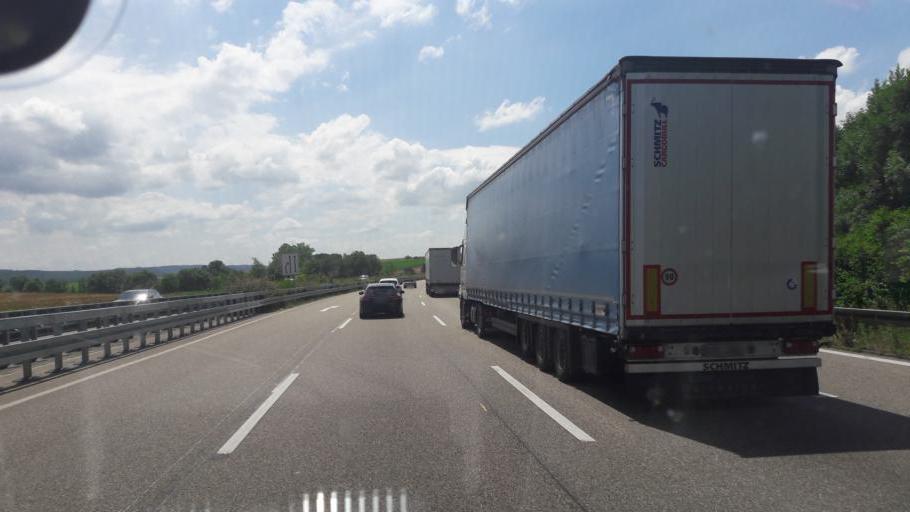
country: DE
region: Baden-Wuerttemberg
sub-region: Regierungsbezirk Stuttgart
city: Bretzfeld
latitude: 49.1831
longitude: 9.4151
